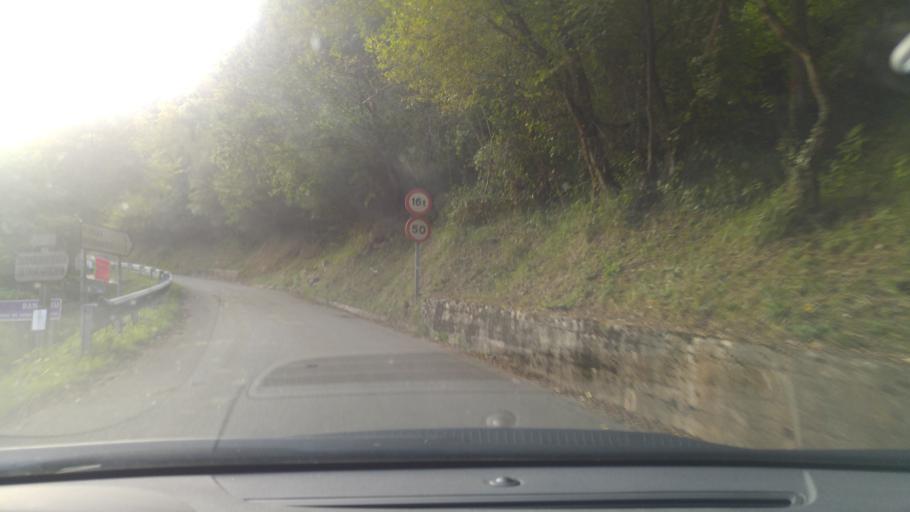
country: ES
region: Asturias
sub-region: Province of Asturias
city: Proaza
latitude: 43.2463
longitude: -6.0347
